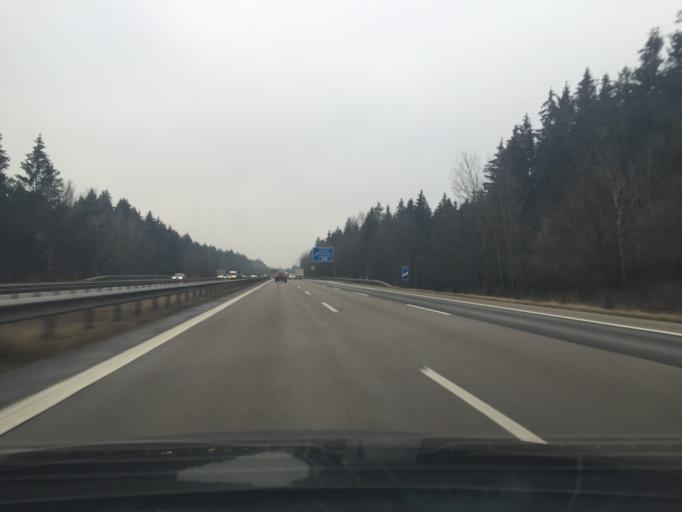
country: DE
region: Bavaria
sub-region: Upper Bavaria
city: Valley
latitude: 47.8879
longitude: 11.7398
